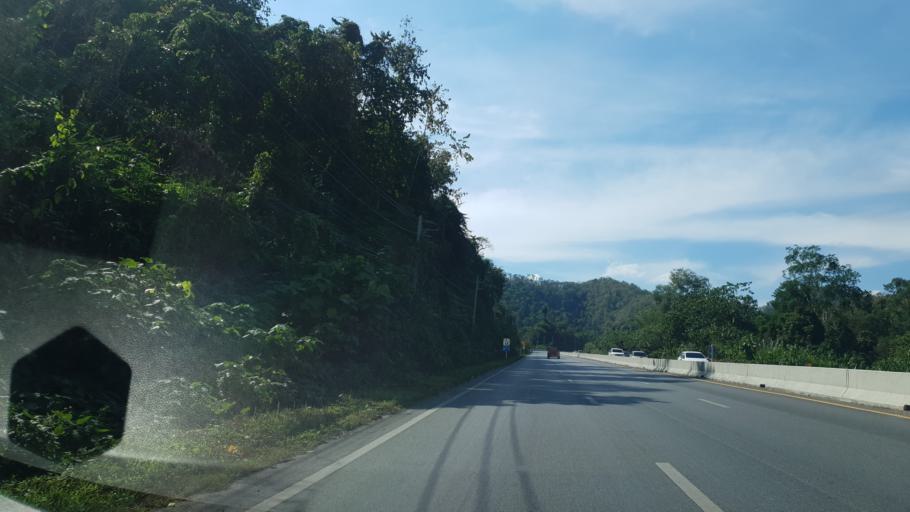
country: TH
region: Phrae
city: Den Chai
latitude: 17.8220
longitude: 100.0845
